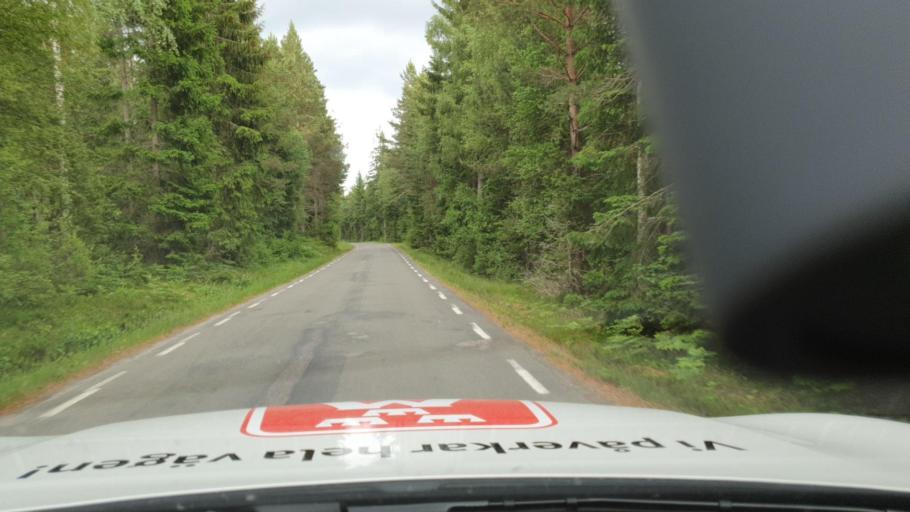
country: SE
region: Vaestra Goetaland
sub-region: Tidaholms Kommun
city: Olofstorp
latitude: 58.1788
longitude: 14.1420
